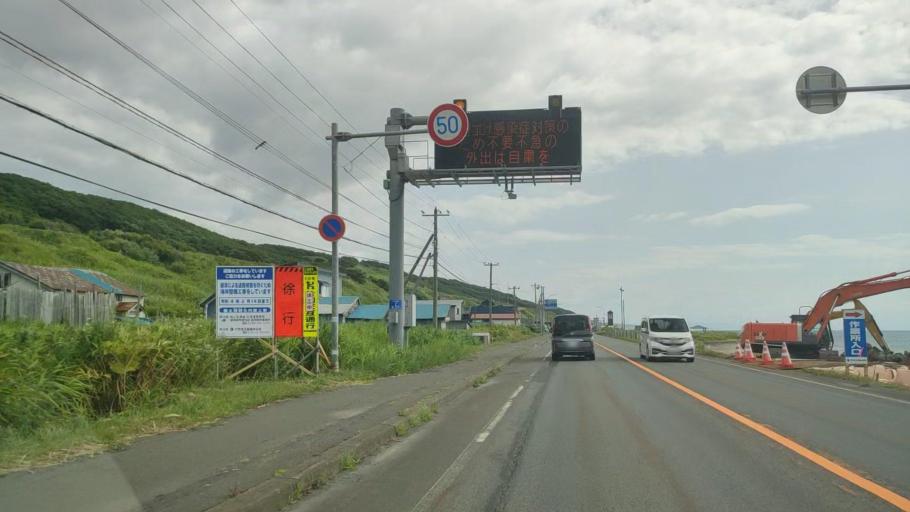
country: JP
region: Hokkaido
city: Rumoi
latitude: 44.1396
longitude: 141.6541
